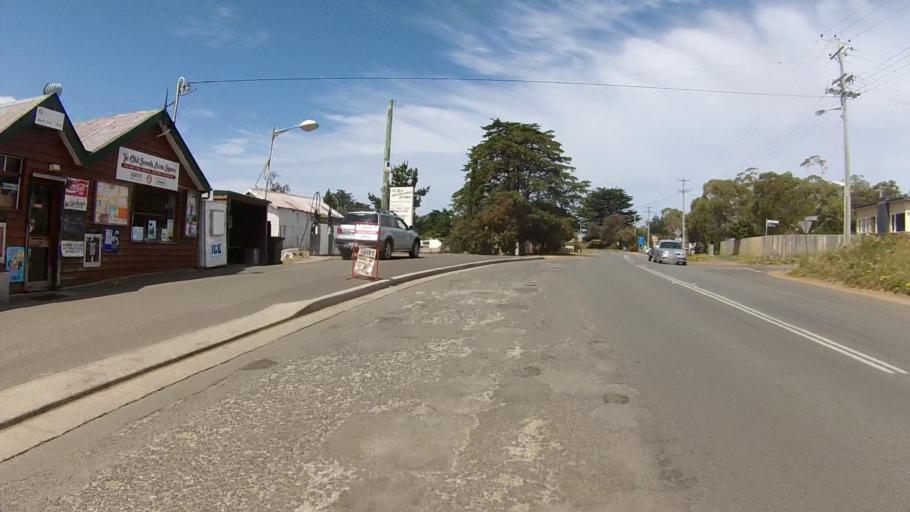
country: AU
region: Tasmania
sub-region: Kingborough
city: Blackmans Bay
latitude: -43.0278
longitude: 147.4165
